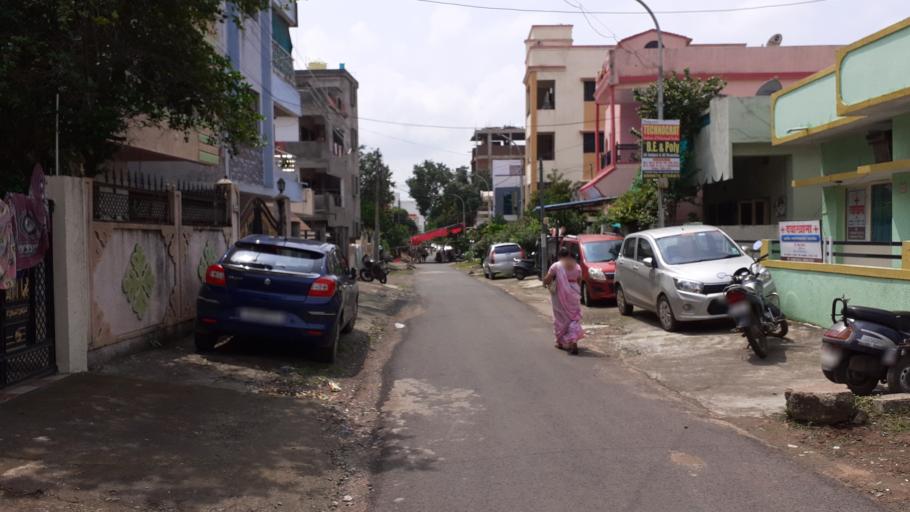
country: IN
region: Maharashtra
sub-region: Nagpur Division
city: Nagpur
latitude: 21.1047
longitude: 79.1145
